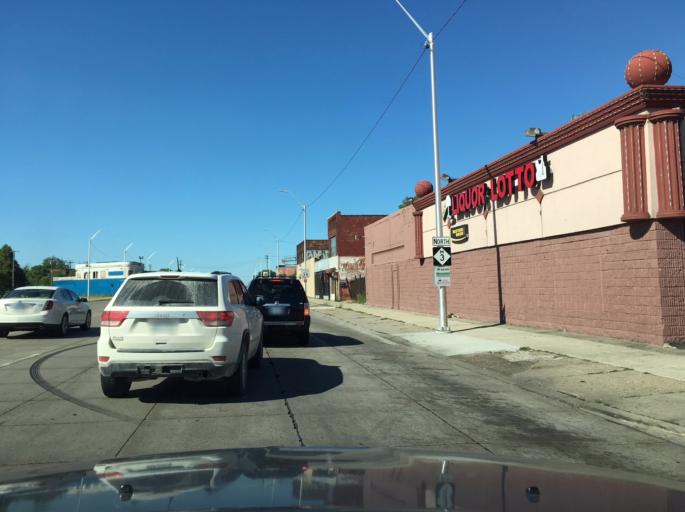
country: US
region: Michigan
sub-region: Wayne County
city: Hamtramck
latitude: 42.3649
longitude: -83.0237
